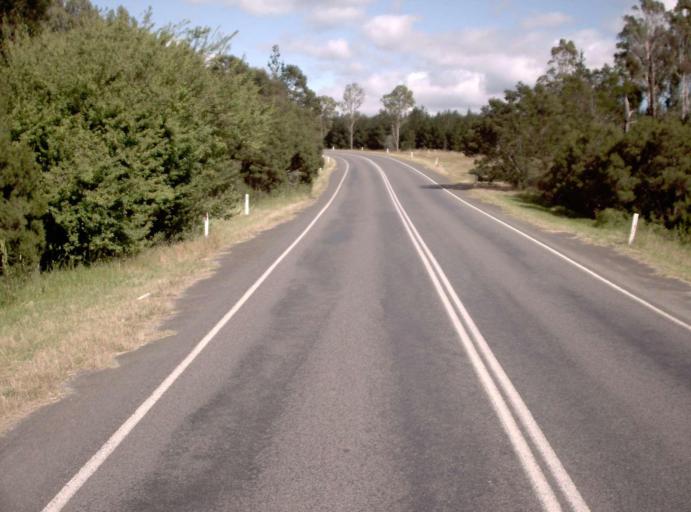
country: AU
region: Victoria
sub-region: Latrobe
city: Traralgon
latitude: -38.1879
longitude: 146.4844
